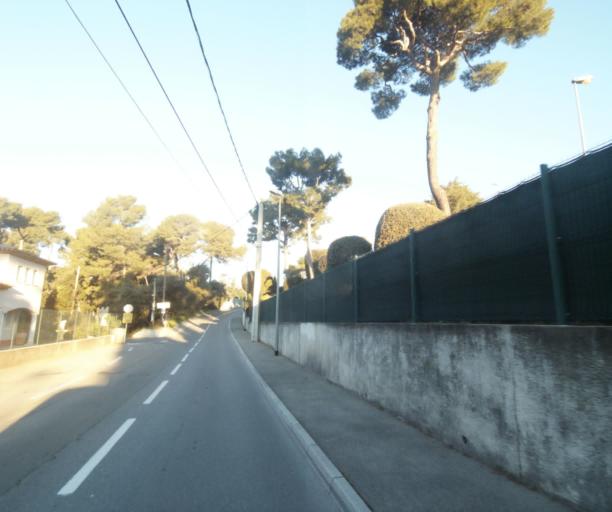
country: FR
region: Provence-Alpes-Cote d'Azur
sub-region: Departement des Alpes-Maritimes
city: Vallauris
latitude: 43.5806
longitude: 7.0827
